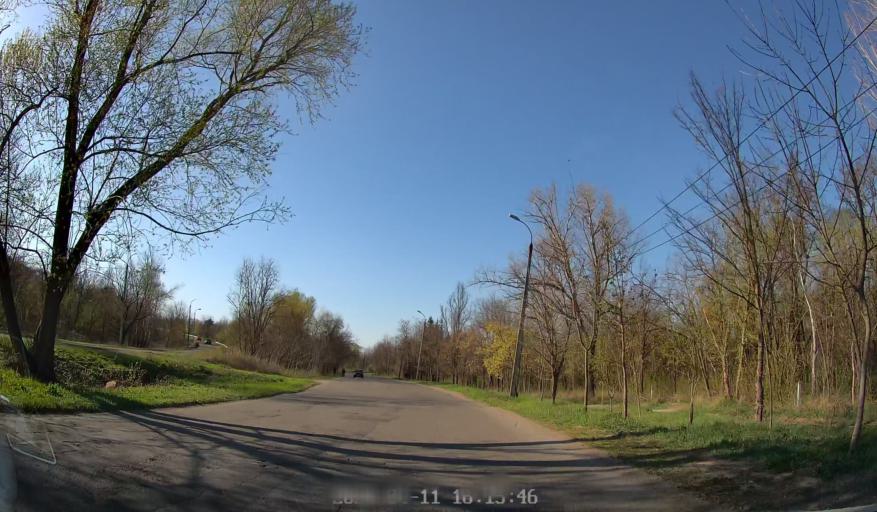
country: MD
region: Chisinau
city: Vadul lui Voda
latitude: 47.0817
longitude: 29.0917
